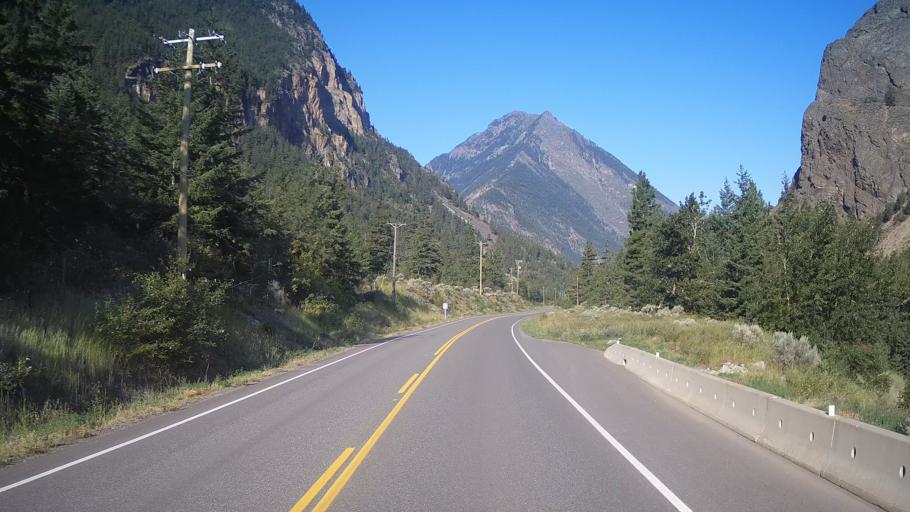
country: CA
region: British Columbia
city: Lillooet
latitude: 50.6701
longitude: -121.9493
